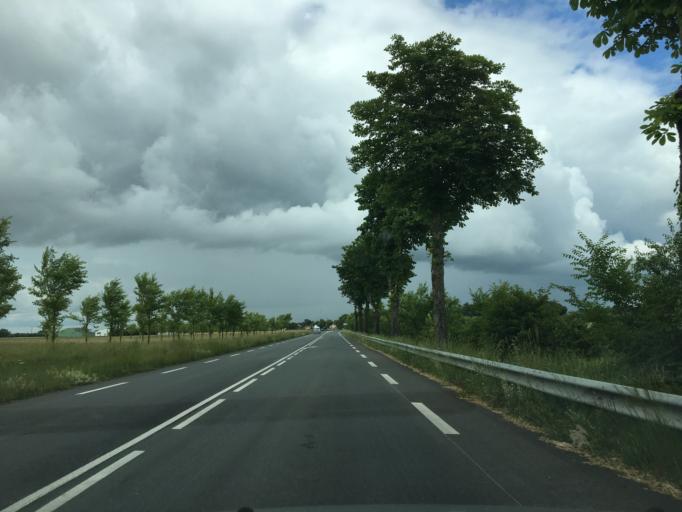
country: FR
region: Poitou-Charentes
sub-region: Departement des Deux-Sevres
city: Beauvoir-sur-Niort
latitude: 46.0846
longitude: -0.5051
